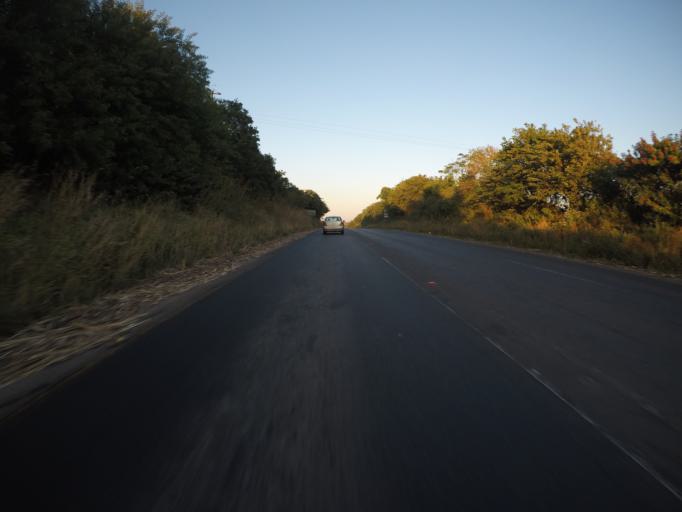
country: ZA
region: KwaZulu-Natal
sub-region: uThungulu District Municipality
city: Empangeni
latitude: -28.8166
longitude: 31.8872
